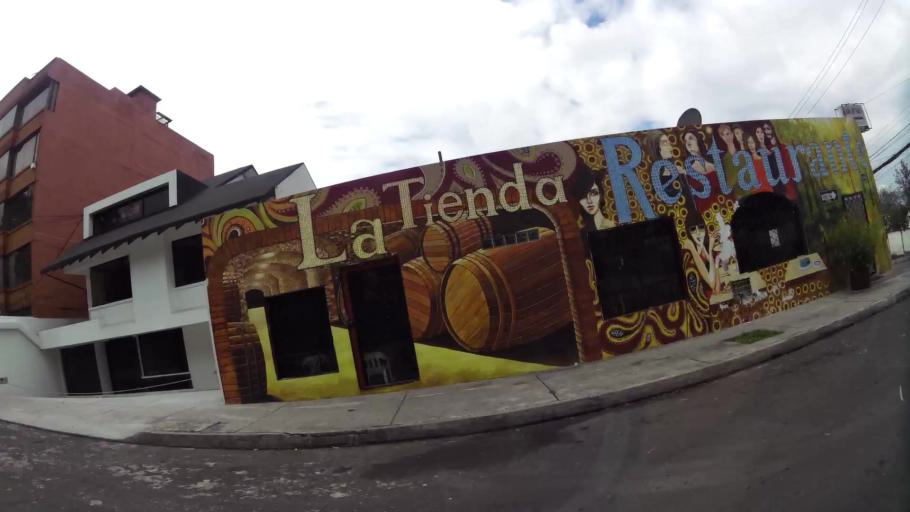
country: EC
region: Pichincha
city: Quito
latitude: -0.1855
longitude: -78.5034
